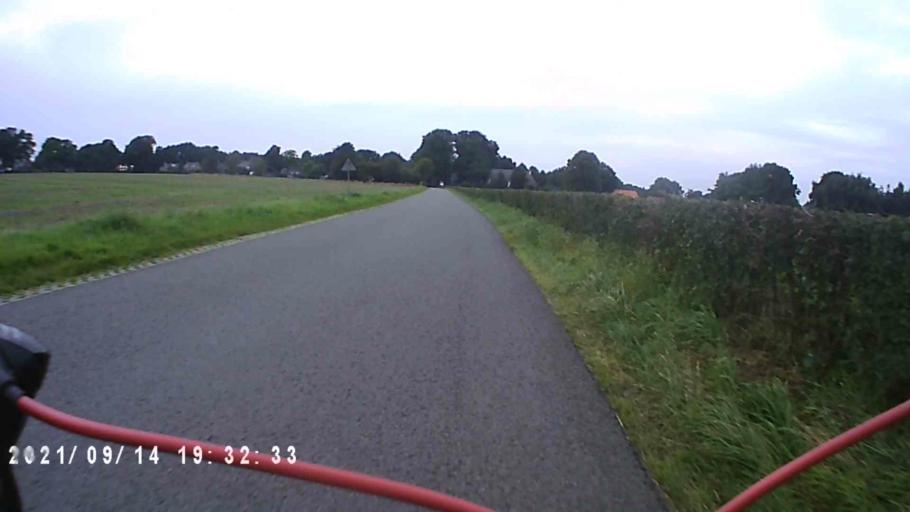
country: NL
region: Drenthe
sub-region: Gemeente Tynaarlo
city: Zuidlaren
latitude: 53.1173
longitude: 6.6731
